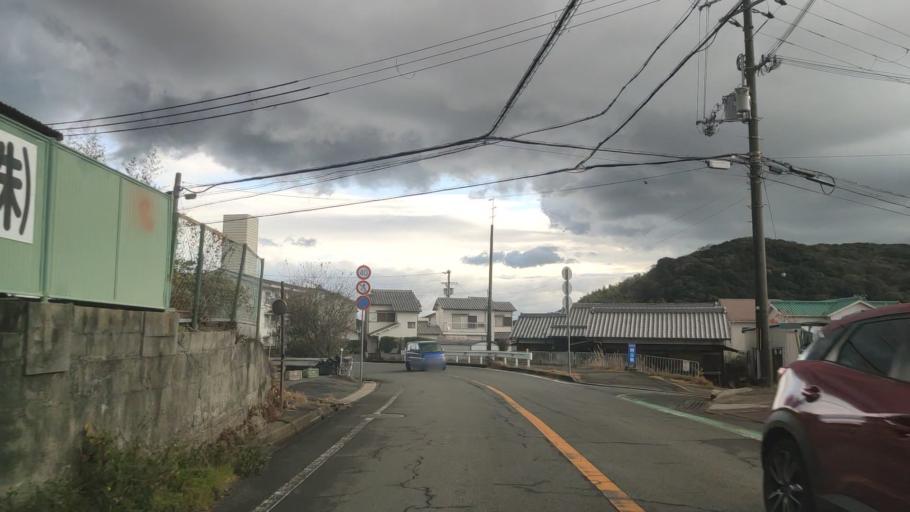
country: JP
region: Hyogo
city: Sumoto
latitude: 34.3276
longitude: 134.8599
